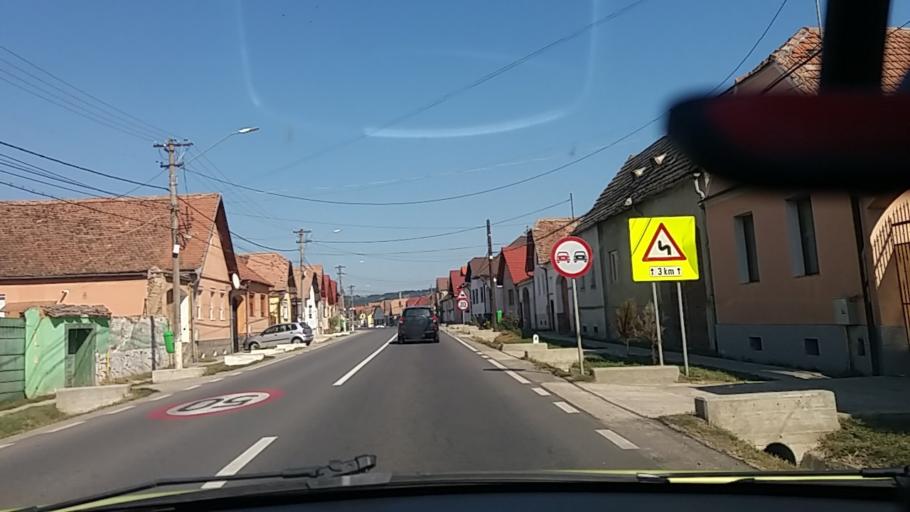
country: RO
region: Sibiu
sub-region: Comuna Sura Mare
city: Sura Mare
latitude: 45.8534
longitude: 24.1686
